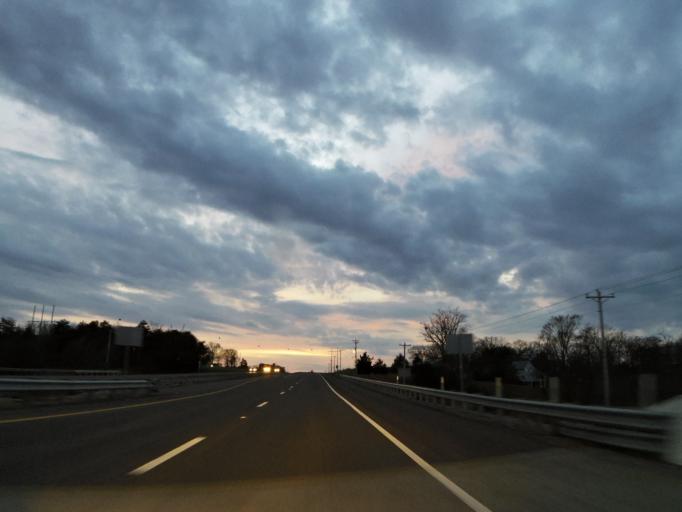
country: US
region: Tennessee
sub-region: Polk County
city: Benton
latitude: 35.2201
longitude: -84.5890
